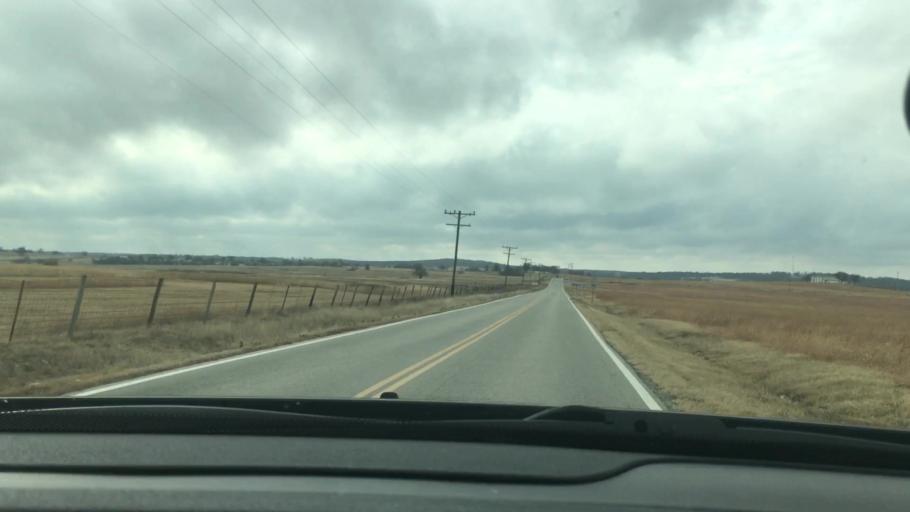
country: US
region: Oklahoma
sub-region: Bryan County
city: Durant
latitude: 34.1045
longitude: -96.4877
